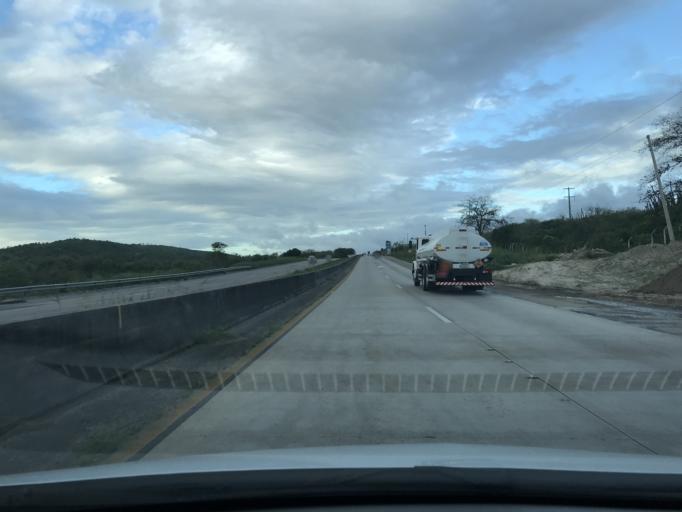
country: BR
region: Pernambuco
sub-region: Caruaru
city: Caruaru
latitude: -8.2980
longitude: -35.9002
